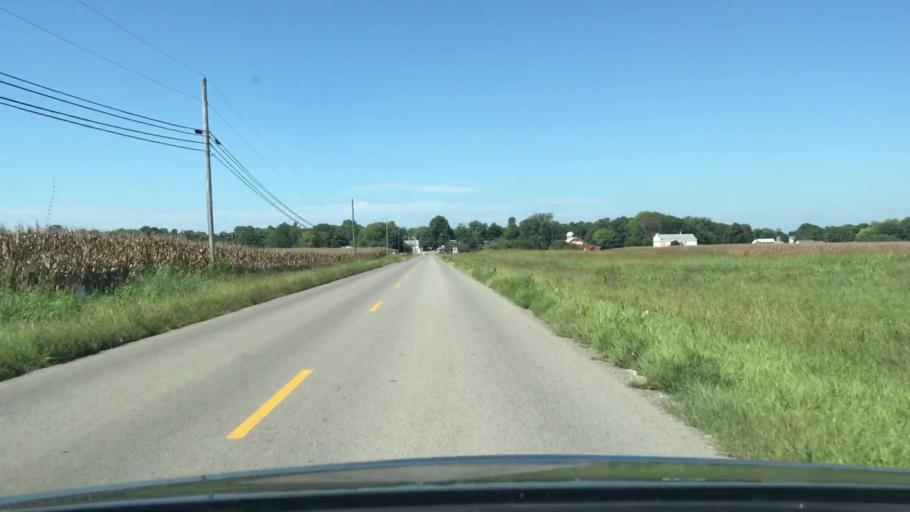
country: US
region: Kentucky
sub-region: Hardin County
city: Elizabethtown
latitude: 37.6017
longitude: -85.8978
